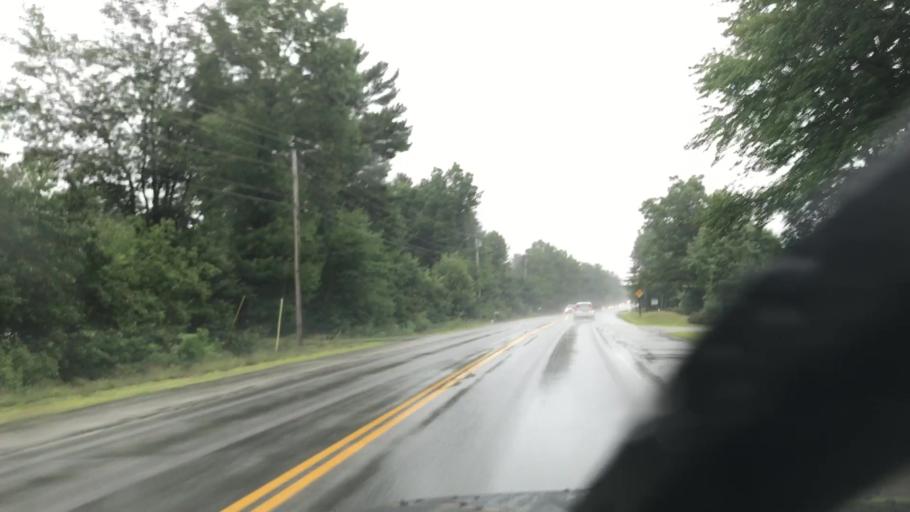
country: US
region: Maine
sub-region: York County
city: Wells Beach Station
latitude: 43.3223
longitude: -70.6424
